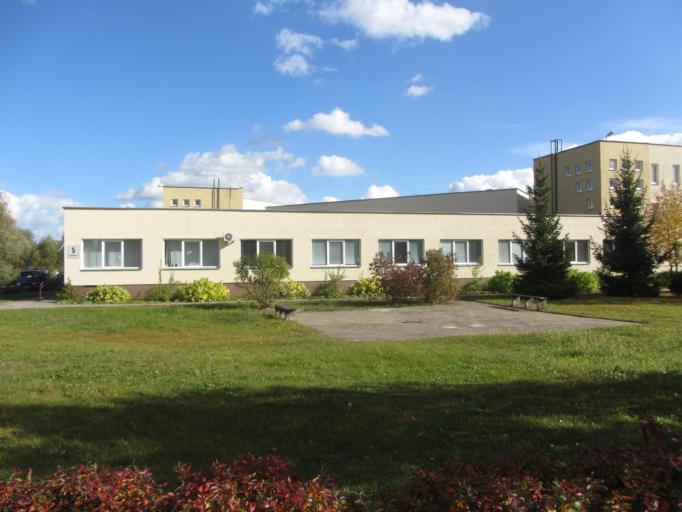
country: LT
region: Utenos apskritis
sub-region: Utena
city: Utena
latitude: 55.4963
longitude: 25.6164
